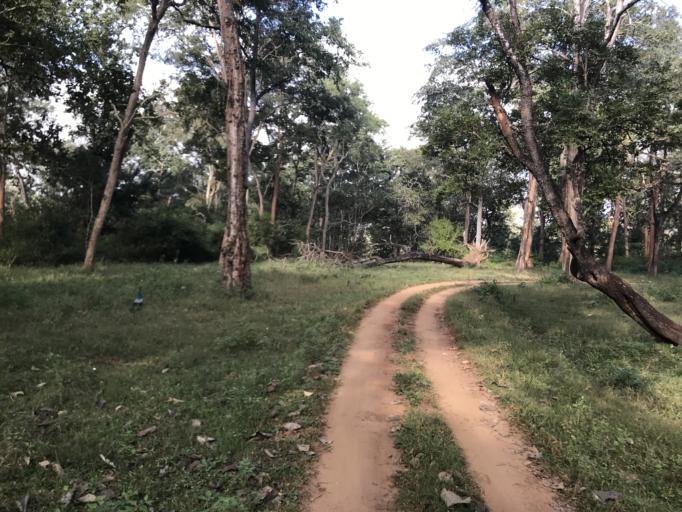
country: IN
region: Karnataka
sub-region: Mysore
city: Heggadadevankote
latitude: 11.9467
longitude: 76.1940
